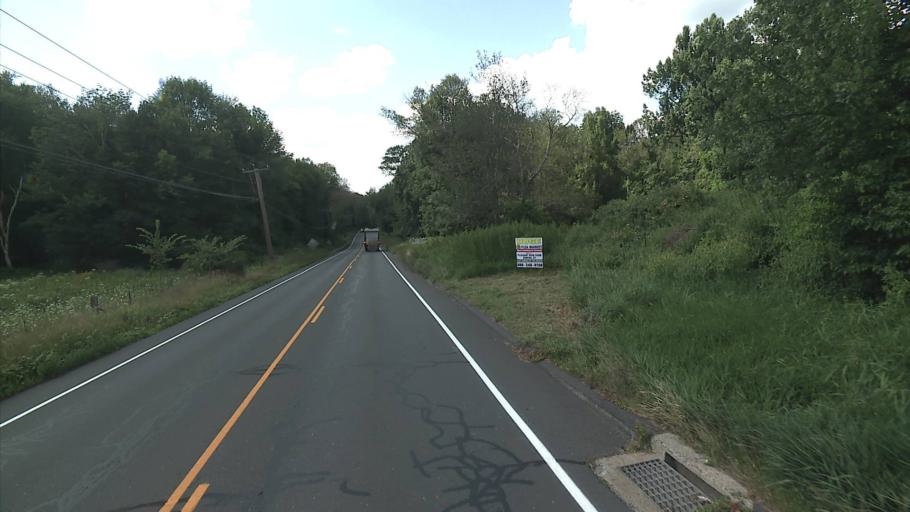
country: US
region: Connecticut
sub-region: Tolland County
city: Somers
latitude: 41.9800
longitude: -72.4051
